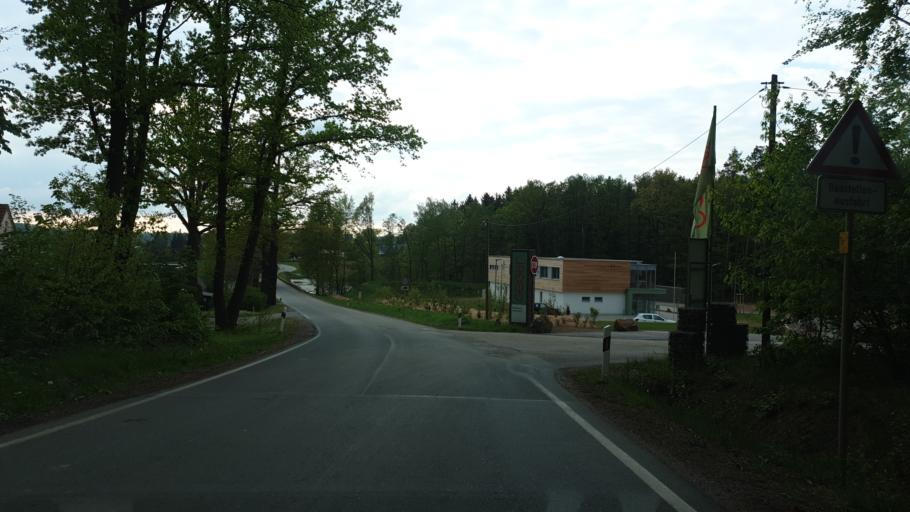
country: DE
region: Saxony
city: Jahnsdorf
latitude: 50.7601
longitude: 12.8465
